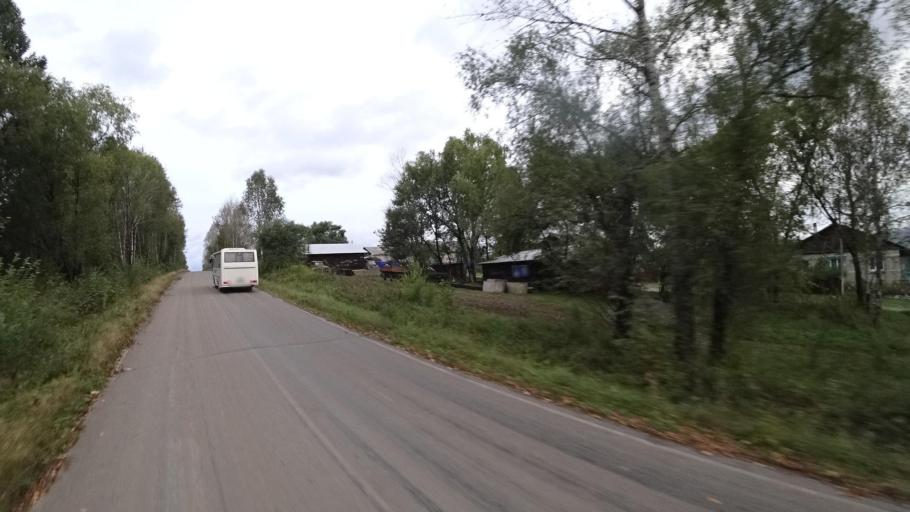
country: RU
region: Jewish Autonomous Oblast
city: Izvestkovyy
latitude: 48.9749
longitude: 131.5746
